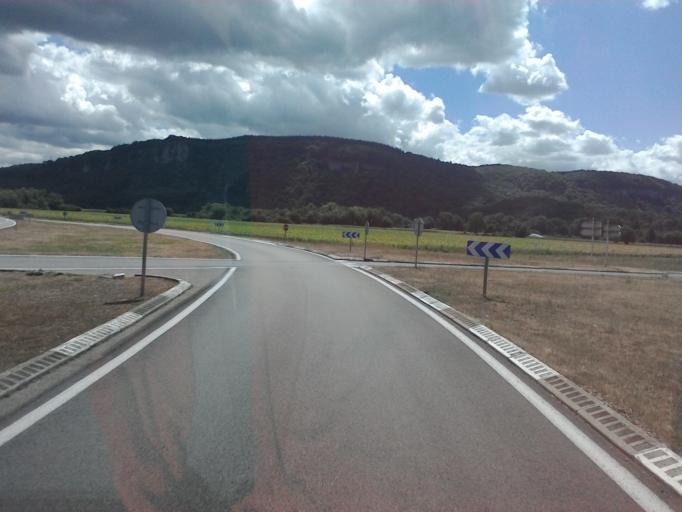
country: FR
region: Rhone-Alpes
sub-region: Departement de l'Ain
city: Lagnieu
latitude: 45.8785
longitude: 5.3477
